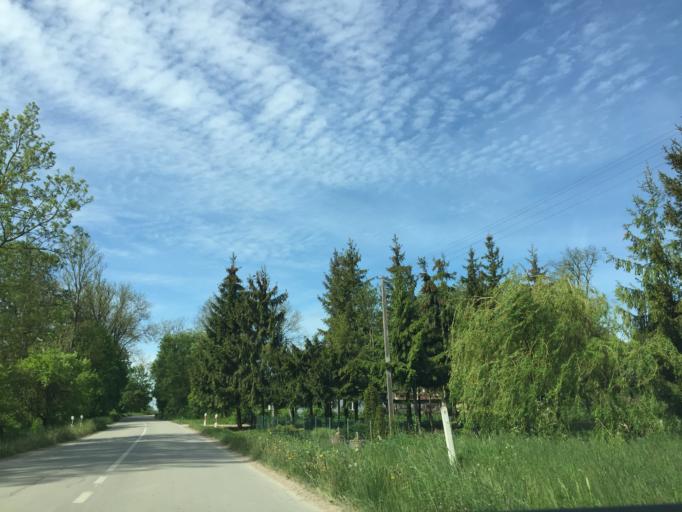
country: LT
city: Linkuva
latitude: 56.1021
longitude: 24.1352
